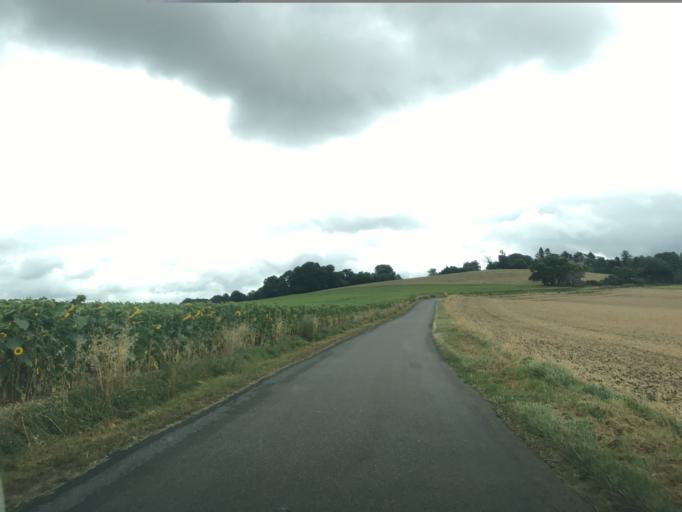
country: FR
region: Poitou-Charentes
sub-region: Departement de la Charente
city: Dignac
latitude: 45.5557
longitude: 0.2589
